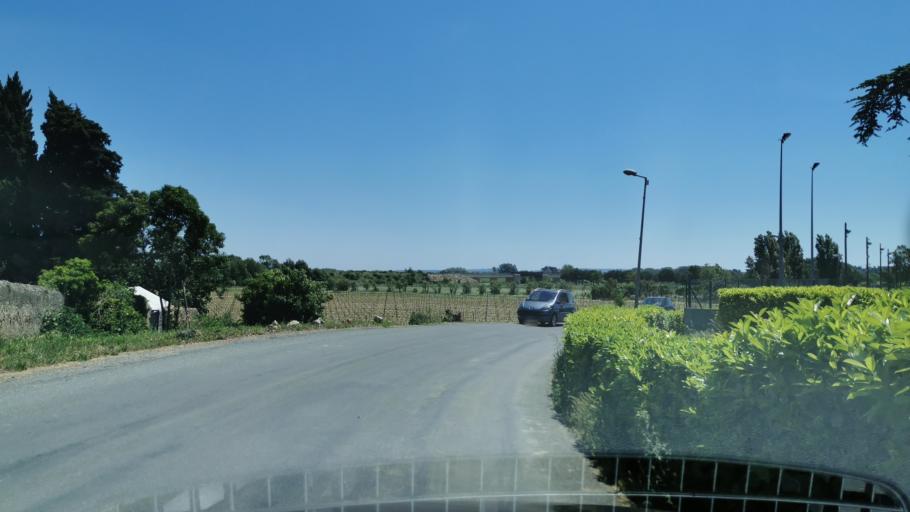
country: FR
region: Languedoc-Roussillon
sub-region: Departement de l'Aude
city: Saint-Marcel-sur-Aude
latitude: 43.2570
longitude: 2.9505
